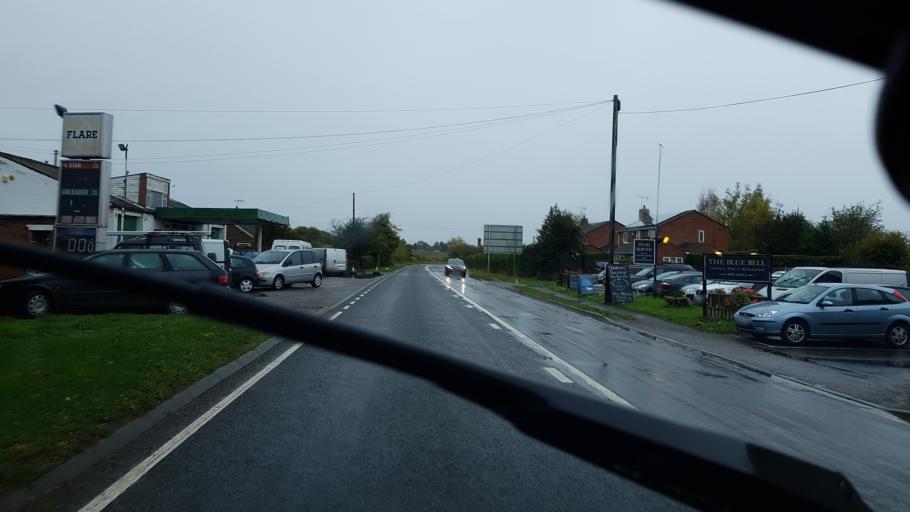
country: GB
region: England
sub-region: Worcestershire
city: Upton upon Severn
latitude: 52.0632
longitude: -2.1948
